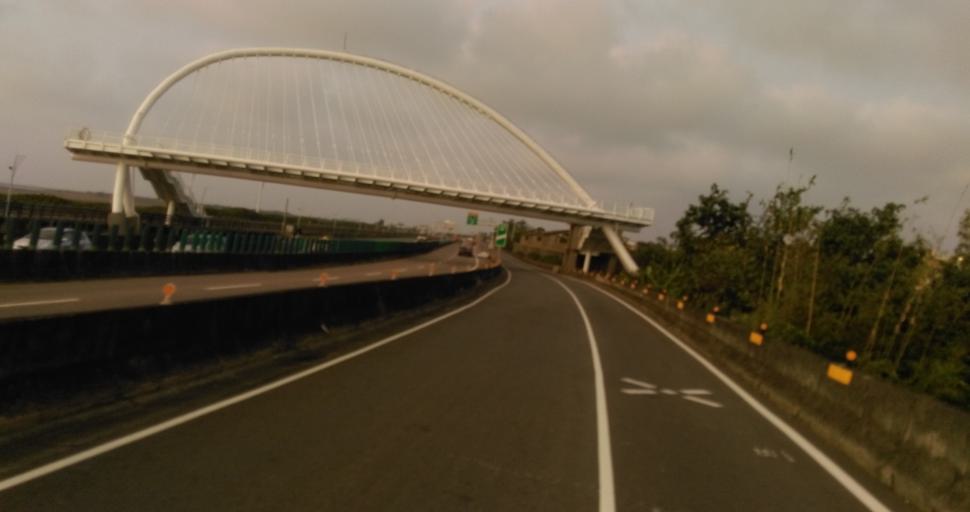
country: TW
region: Taiwan
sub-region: Hsinchu
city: Hsinchu
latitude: 24.7481
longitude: 120.9039
